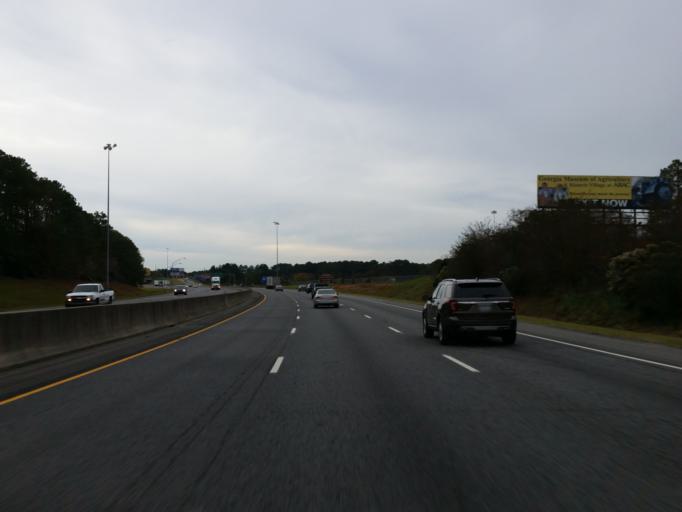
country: US
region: Georgia
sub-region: Tift County
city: Tifton
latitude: 31.4698
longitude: -83.5279
